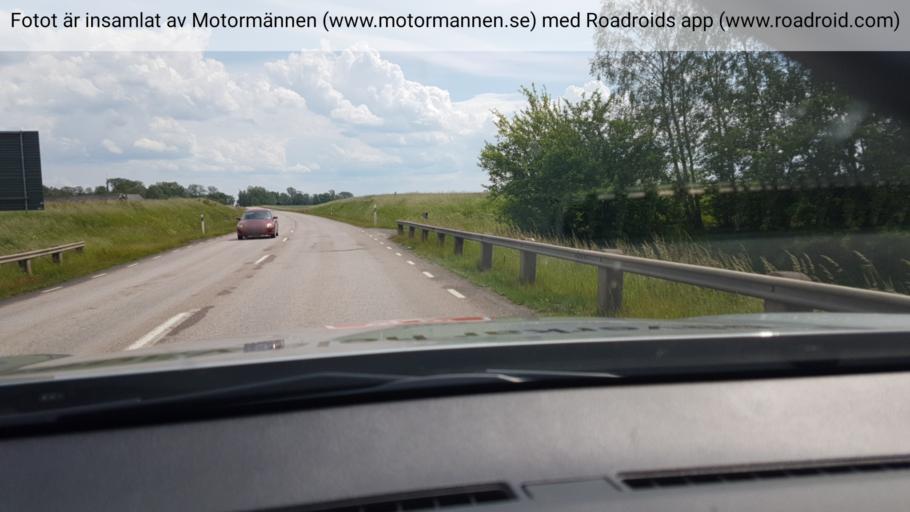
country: SE
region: Vaestra Goetaland
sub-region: Skovde Kommun
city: Skoevde
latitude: 58.3941
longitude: 13.9286
